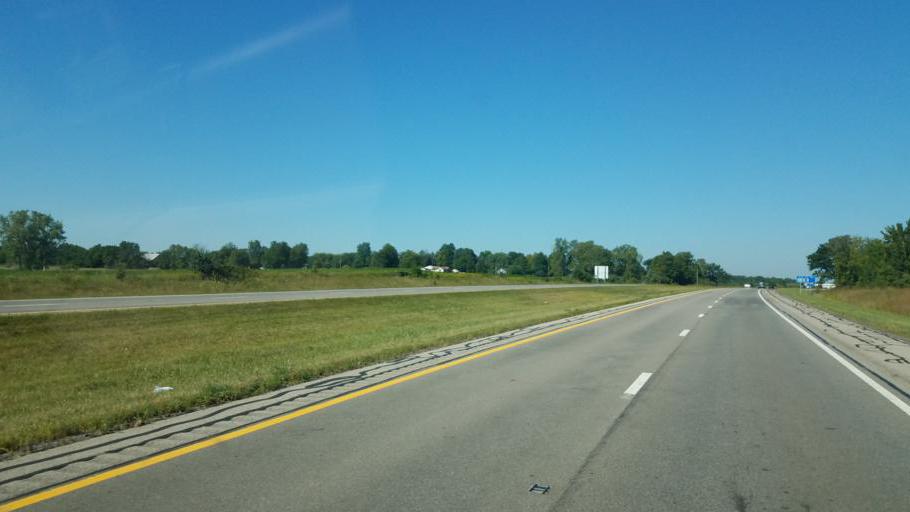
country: US
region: Ohio
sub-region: Crawford County
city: Galion
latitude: 40.7609
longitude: -82.7688
